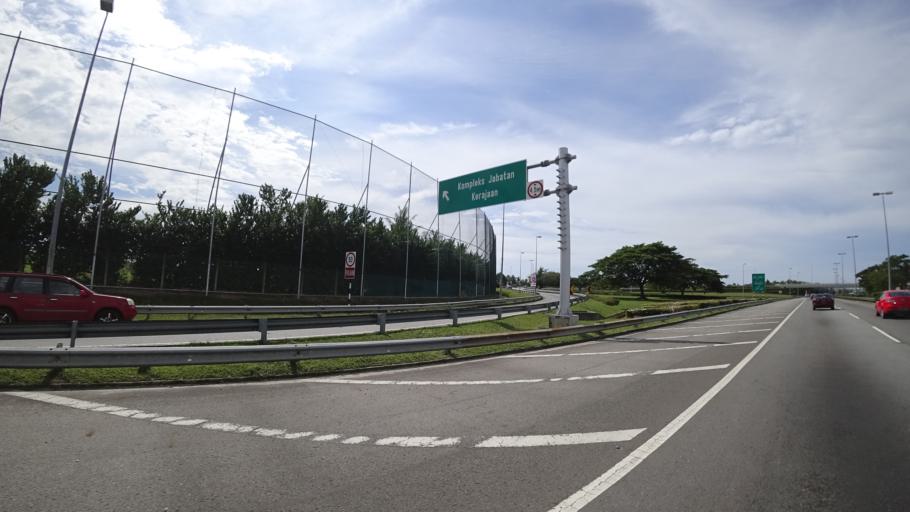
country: BN
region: Brunei and Muara
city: Bandar Seri Begawan
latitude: 4.9262
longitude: 114.9227
